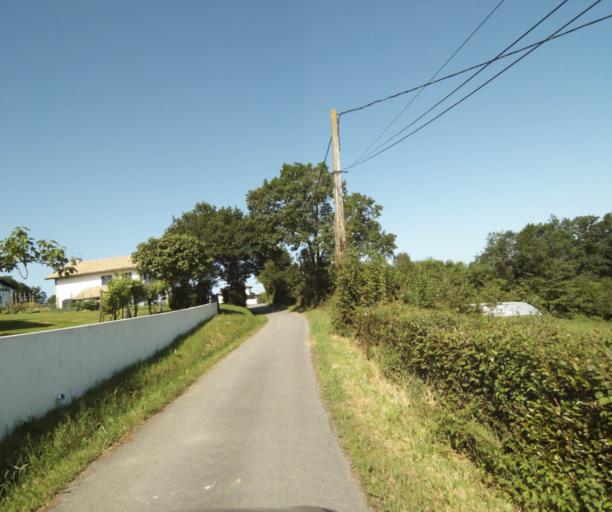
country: FR
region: Aquitaine
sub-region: Departement des Pyrenees-Atlantiques
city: Villefranque
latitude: 43.4527
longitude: -1.4452
